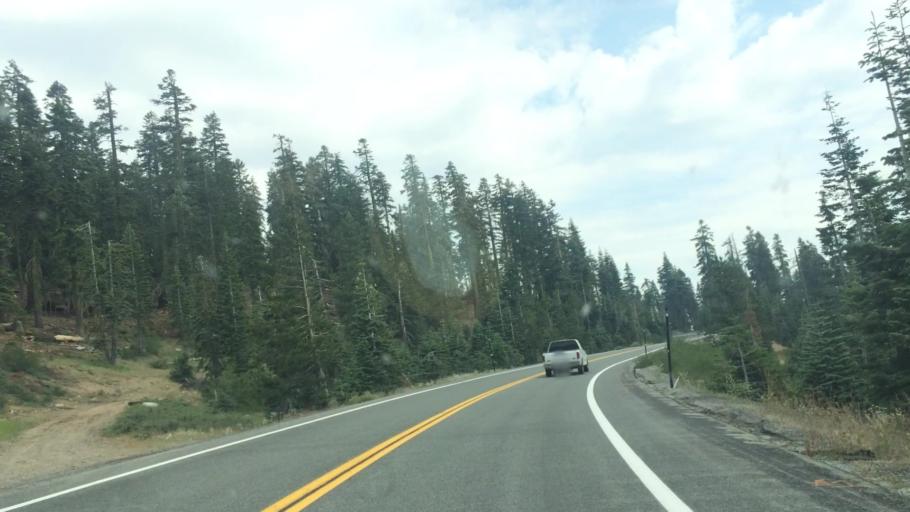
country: US
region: California
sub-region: El Dorado County
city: South Lake Tahoe
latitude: 38.6270
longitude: -120.2049
